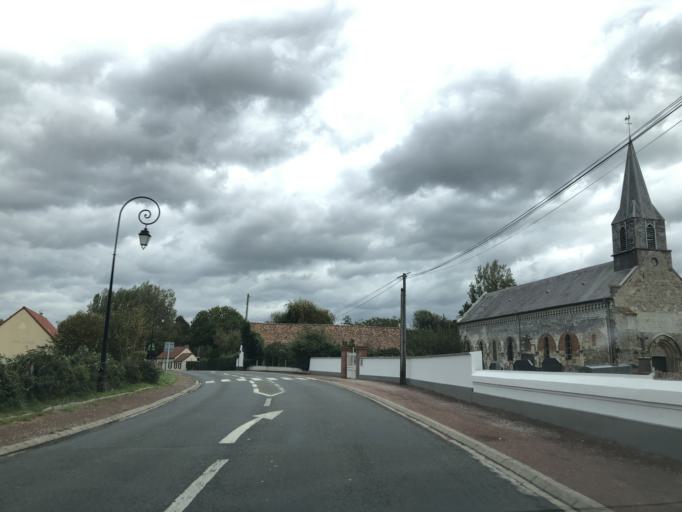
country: FR
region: Nord-Pas-de-Calais
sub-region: Departement du Pas-de-Calais
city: Groffliers
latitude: 50.3830
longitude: 1.6214
